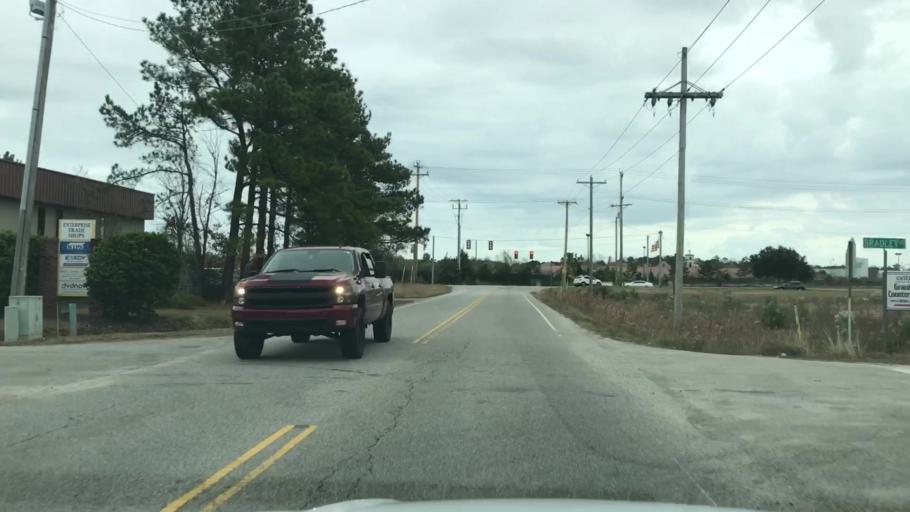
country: US
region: South Carolina
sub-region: Horry County
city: Forestbrook
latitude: 33.7151
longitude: -78.9383
